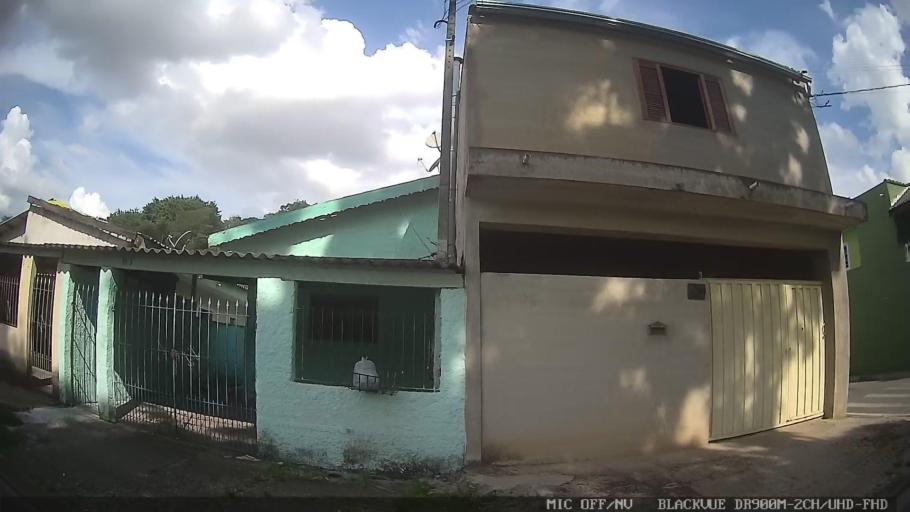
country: BR
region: Sao Paulo
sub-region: Atibaia
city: Atibaia
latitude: -23.1249
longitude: -46.5772
